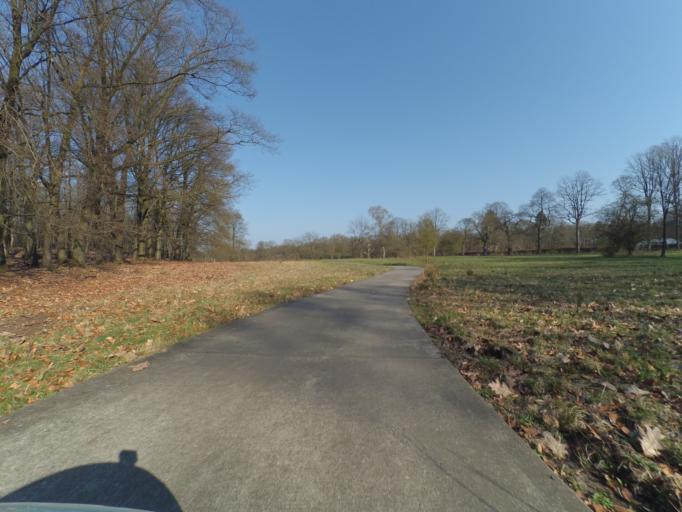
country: NL
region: Gelderland
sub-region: Gemeente Arnhem
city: Hoogkamp
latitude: 52.0384
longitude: 5.8537
